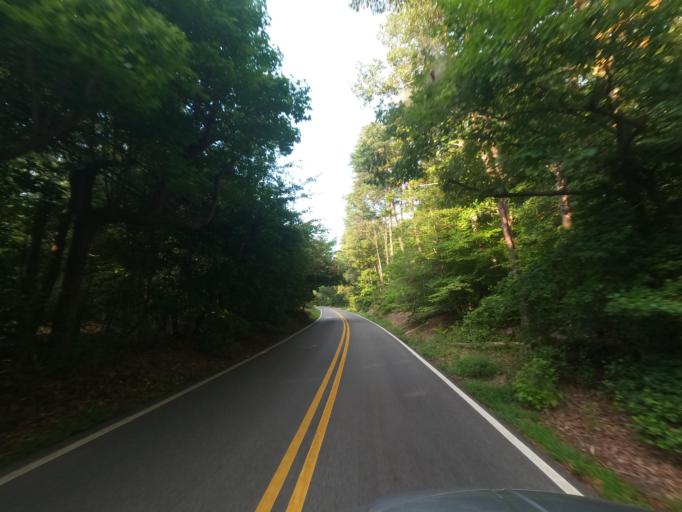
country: US
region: Maryland
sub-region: Prince George's County
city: Accokeek
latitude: 38.6795
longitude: -77.0191
